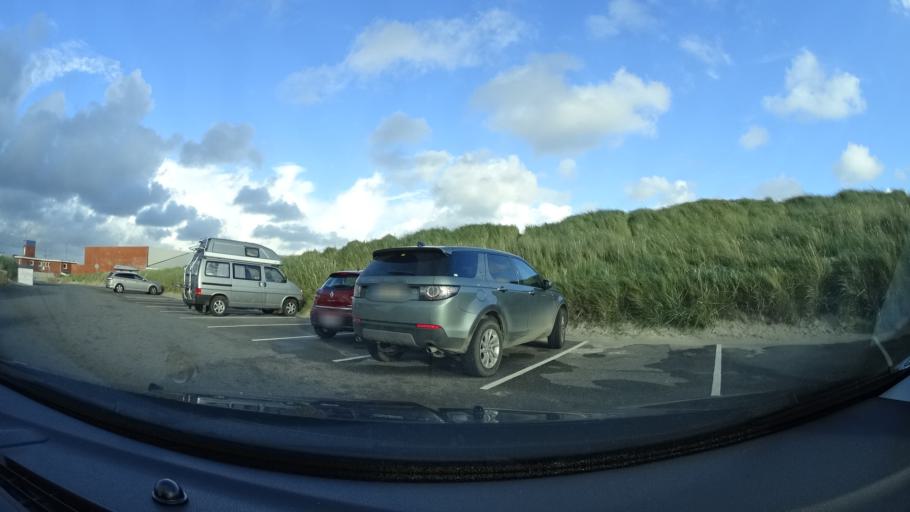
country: DK
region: Central Jutland
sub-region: Ringkobing-Skjern Kommune
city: Hvide Sande
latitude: 55.9987
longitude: 8.1205
